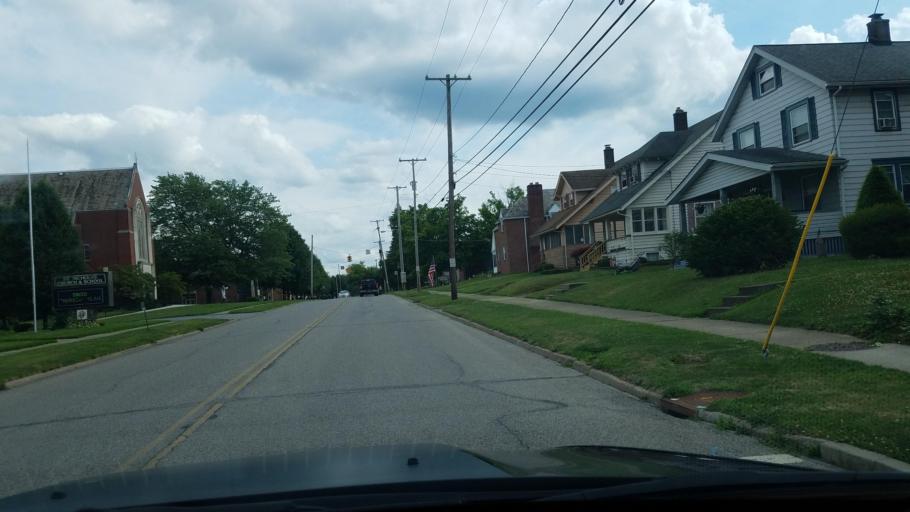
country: US
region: Ohio
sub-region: Mahoning County
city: Struthers
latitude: 41.0508
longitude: -80.6036
